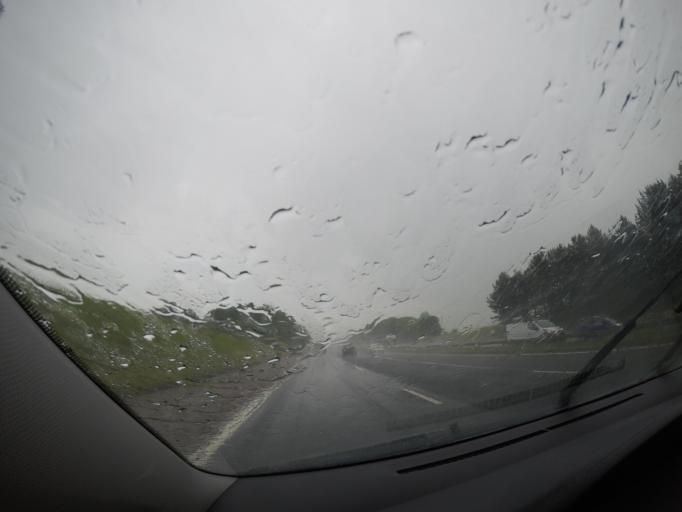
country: GB
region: England
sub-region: Cumbria
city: Penrith
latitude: 54.6947
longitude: -2.7919
